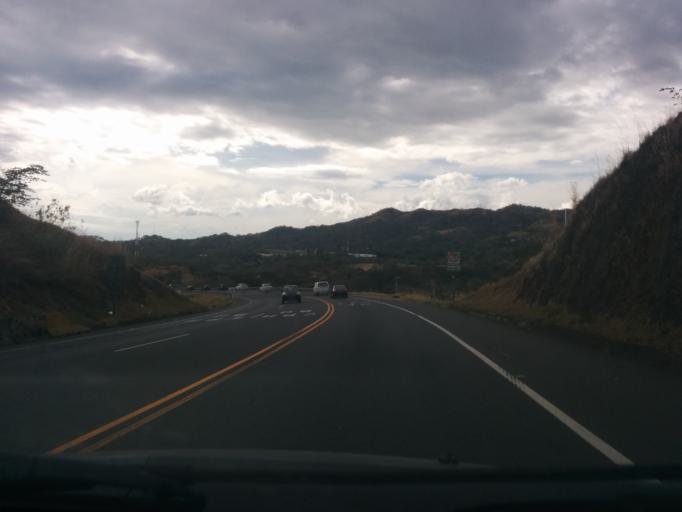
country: CR
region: Alajuela
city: Atenas
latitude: 9.9654
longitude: -84.3419
